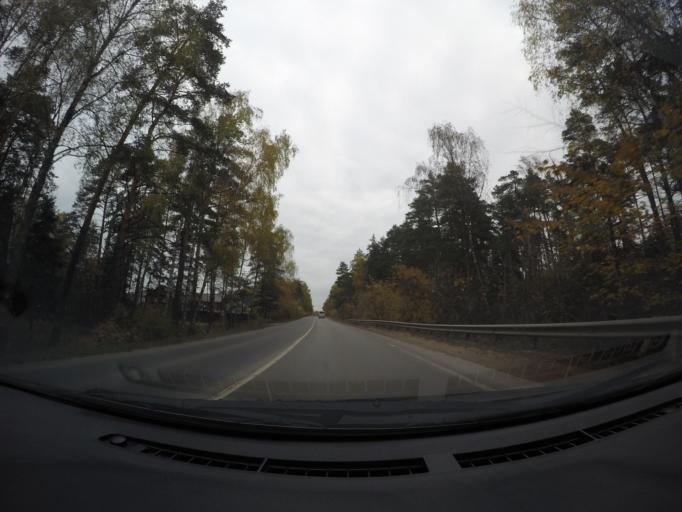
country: RU
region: Moskovskaya
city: Obukhovo
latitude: 55.7771
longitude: 38.2460
